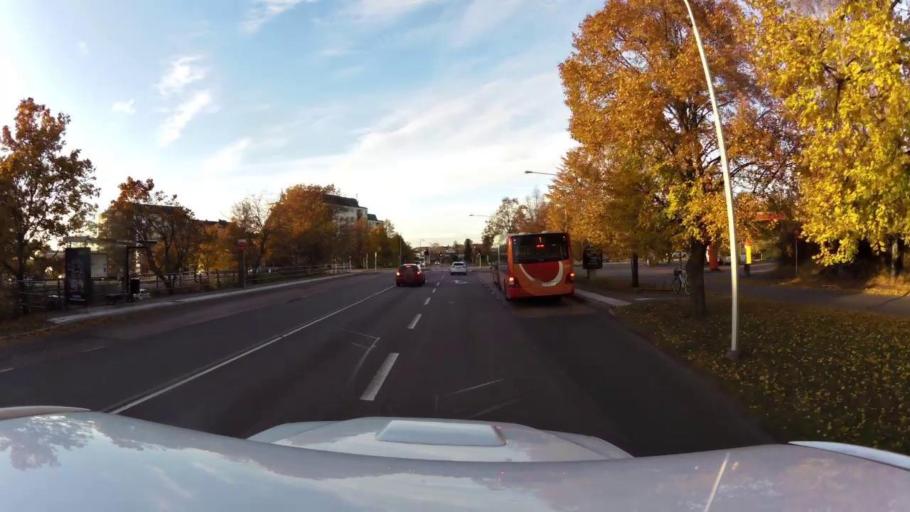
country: SE
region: OEstergoetland
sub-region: Linkopings Kommun
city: Linkoping
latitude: 58.3928
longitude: 15.6462
